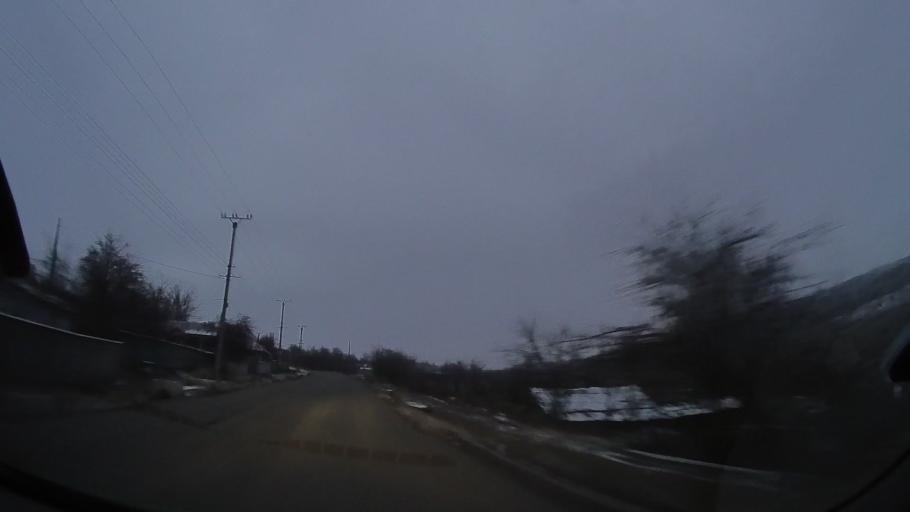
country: RO
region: Vaslui
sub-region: Comuna Vutcani
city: Vutcani
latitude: 46.4092
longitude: 27.9945
